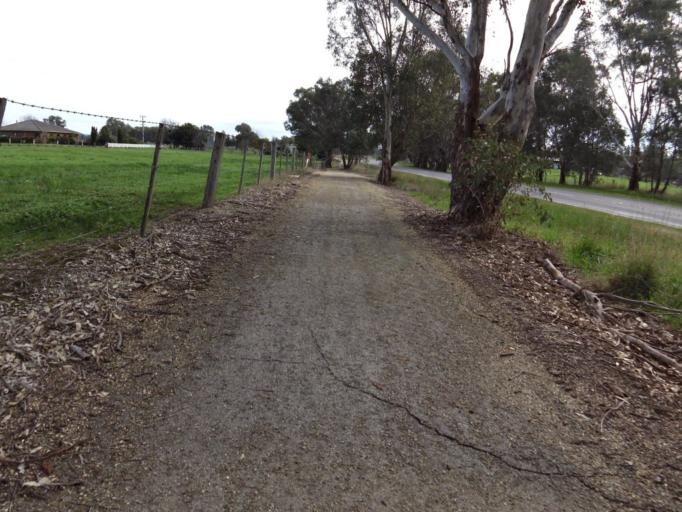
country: AU
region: Victoria
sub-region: Wangaratta
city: Wangaratta
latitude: -36.4054
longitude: 146.3487
